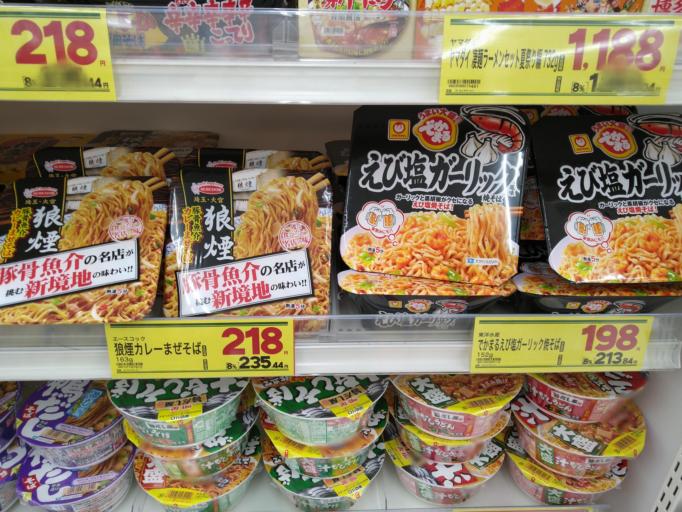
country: JP
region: Kyoto
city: Ayabe
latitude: 35.3015
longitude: 135.2442
